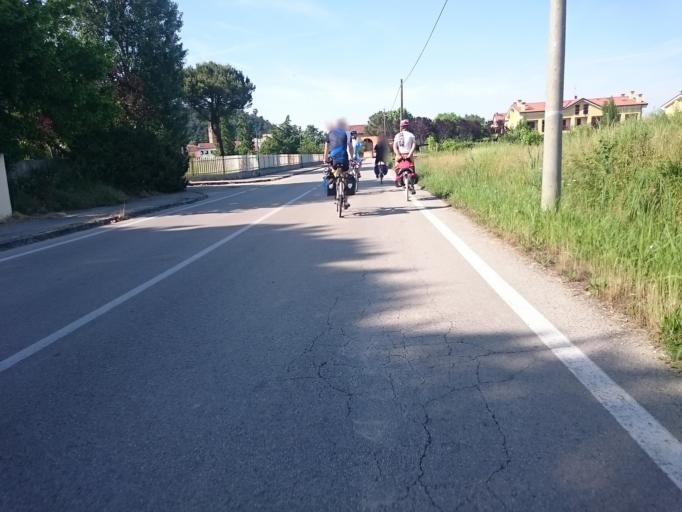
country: IT
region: Veneto
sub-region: Provincia di Padova
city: Torreglia
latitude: 45.3469
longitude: 11.7593
